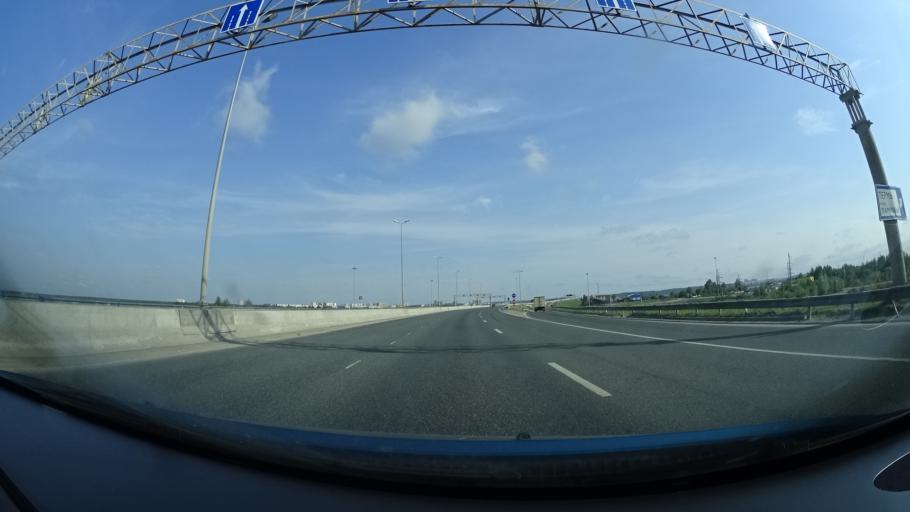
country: RU
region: Perm
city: Kondratovo
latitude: 58.0063
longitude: 56.0531
